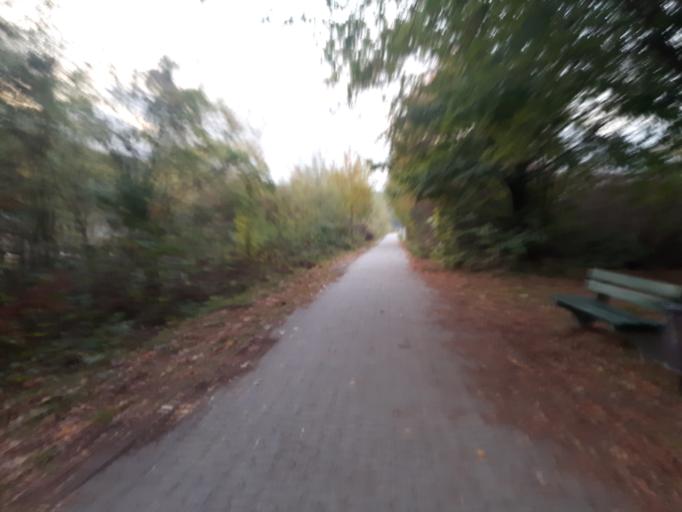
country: DE
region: Rheinland-Pfalz
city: Remagen
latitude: 50.5864
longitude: 7.2215
